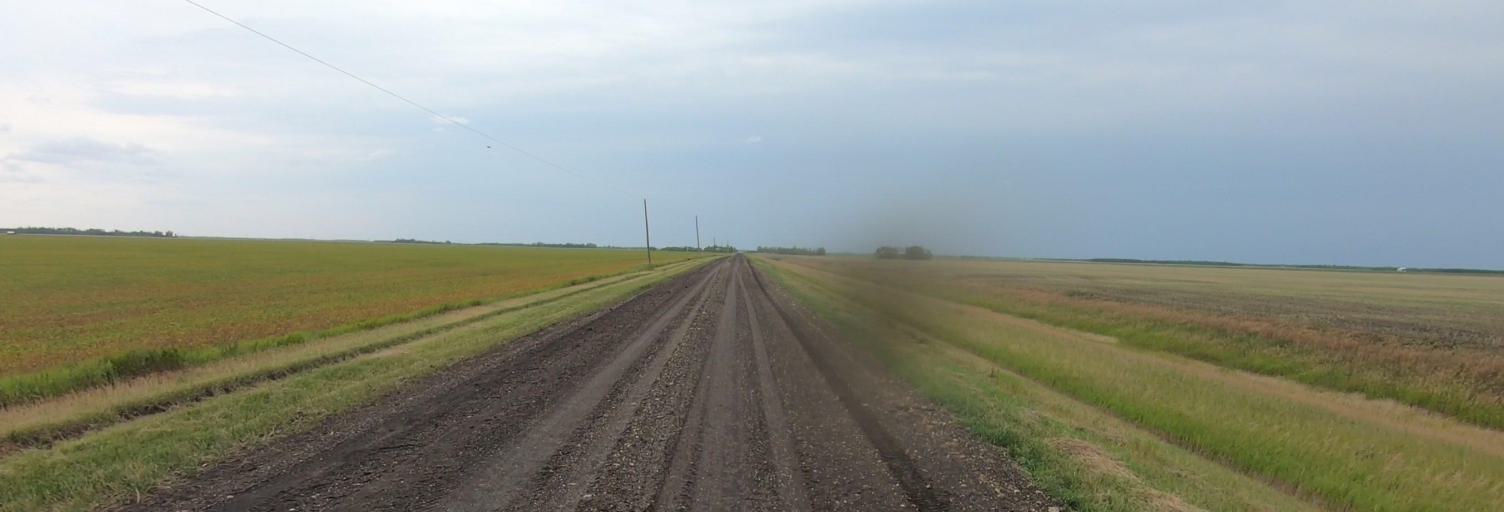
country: CA
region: Manitoba
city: Headingley
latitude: 49.7513
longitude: -97.4135
